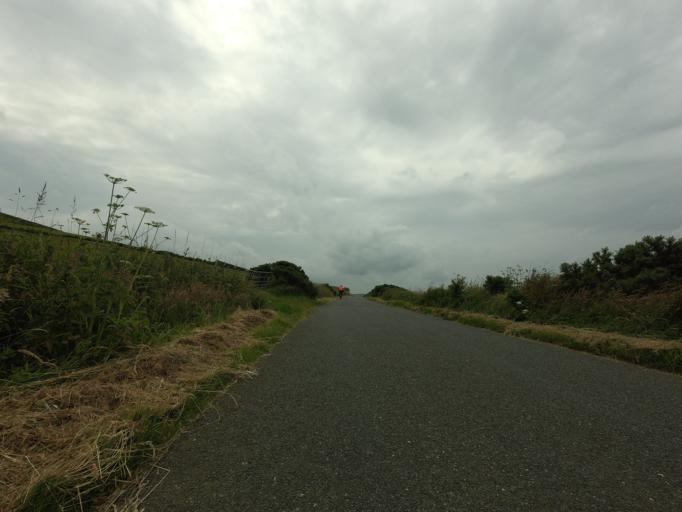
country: GB
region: Scotland
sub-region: Aberdeenshire
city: Portsoy
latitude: 57.6686
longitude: -2.7250
